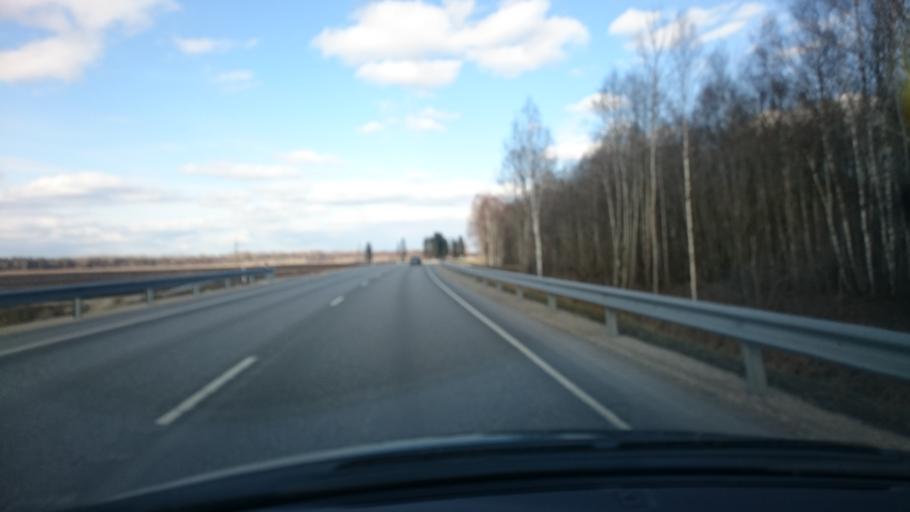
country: EE
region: Laeaene
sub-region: Lihula vald
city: Lihula
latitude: 58.7793
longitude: 23.9955
